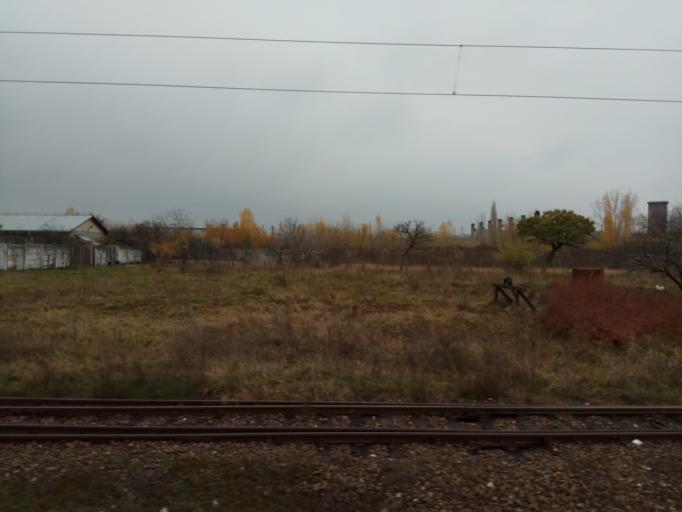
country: RO
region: Prahova
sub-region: Comuna Baba Ana
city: Conduratu
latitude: 44.9927
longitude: 26.4316
